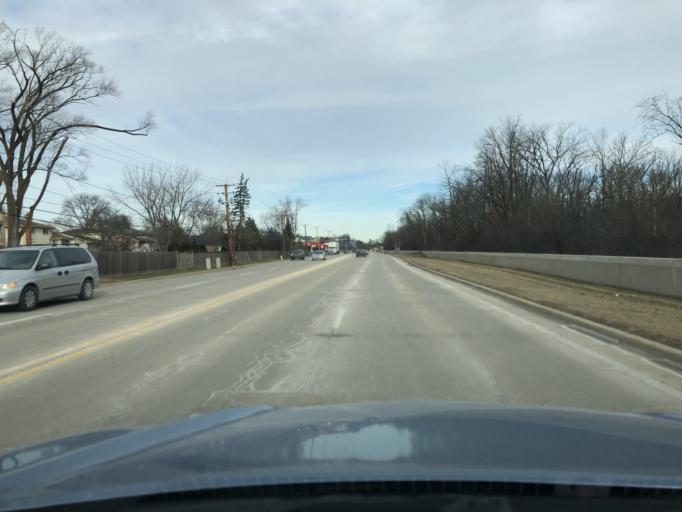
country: US
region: Illinois
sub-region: Cook County
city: Prospect Heights
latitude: 42.0924
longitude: -87.8912
